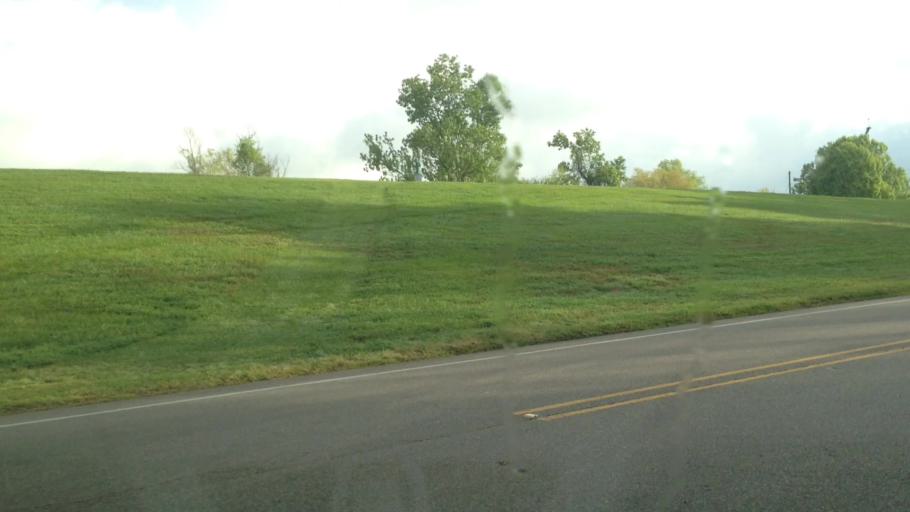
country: US
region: Louisiana
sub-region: Jefferson Parish
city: Jefferson
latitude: 29.9503
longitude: -90.1540
